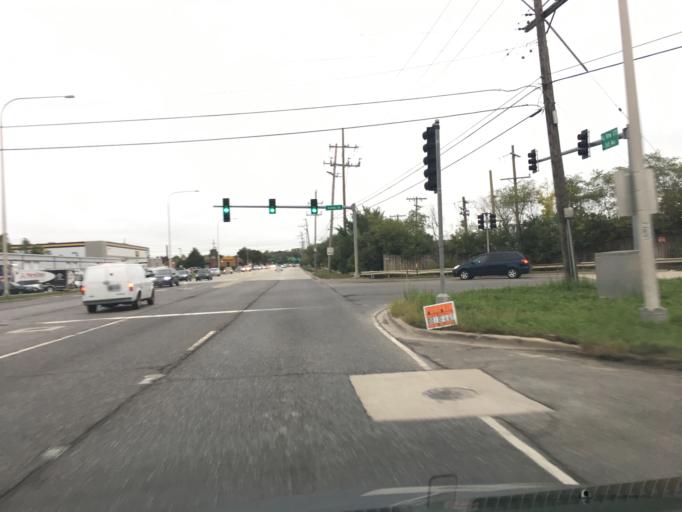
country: US
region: Illinois
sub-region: Cook County
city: Lyons
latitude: 41.8104
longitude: -87.8339
